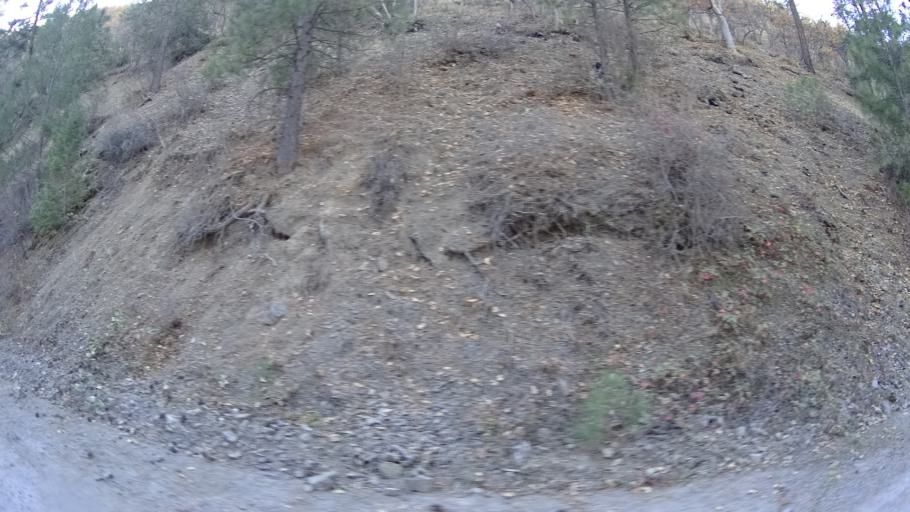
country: US
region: California
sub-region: Siskiyou County
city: Yreka
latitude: 41.8274
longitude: -122.6492
